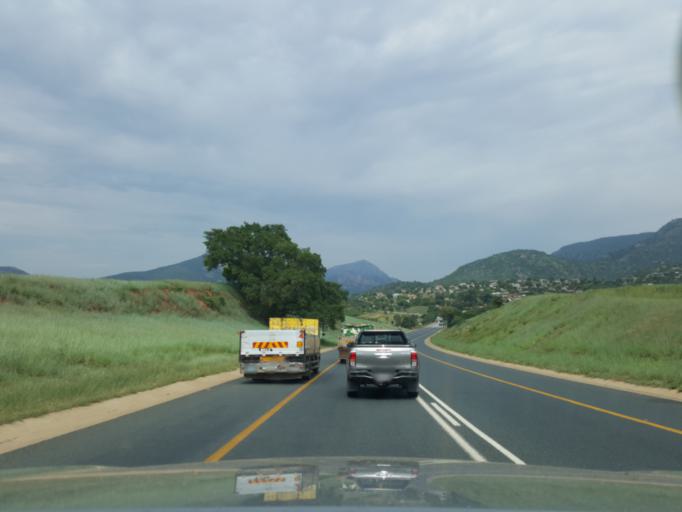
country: SZ
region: Hhohho
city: Ntfonjeni
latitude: -25.5378
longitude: 31.3176
